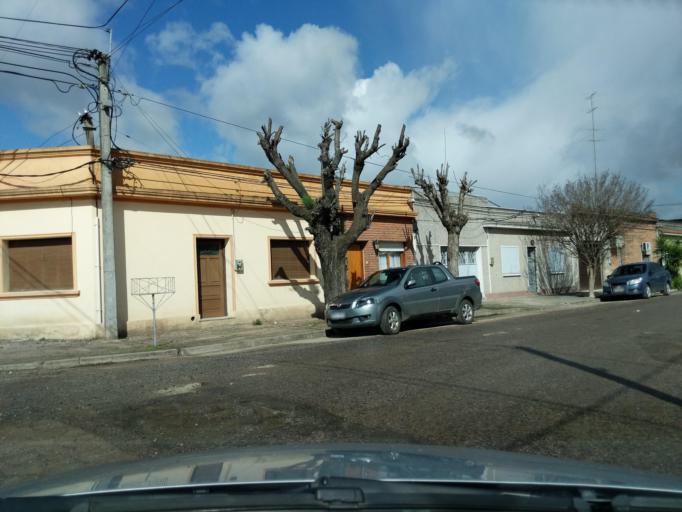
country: UY
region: Florida
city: Florida
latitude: -34.0900
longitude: -56.2180
